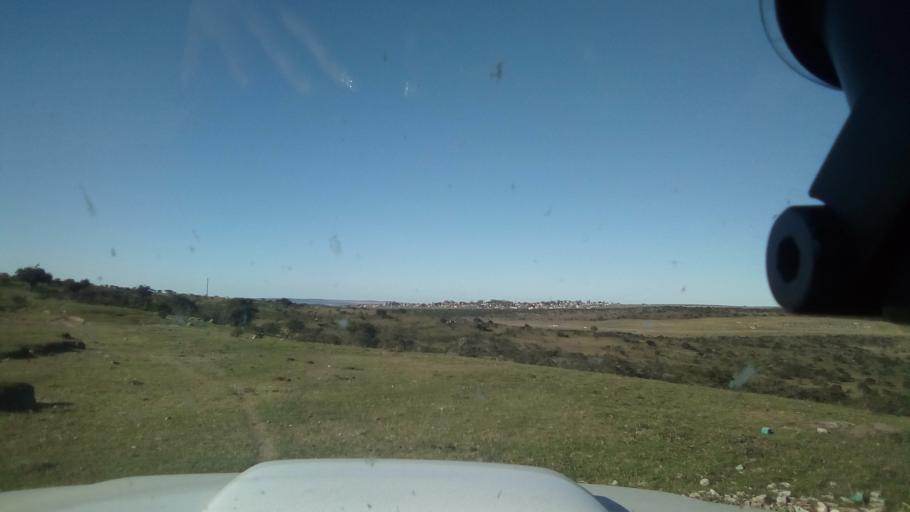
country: ZA
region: Eastern Cape
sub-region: Buffalo City Metropolitan Municipality
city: Bhisho
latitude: -32.9388
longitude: 27.2929
